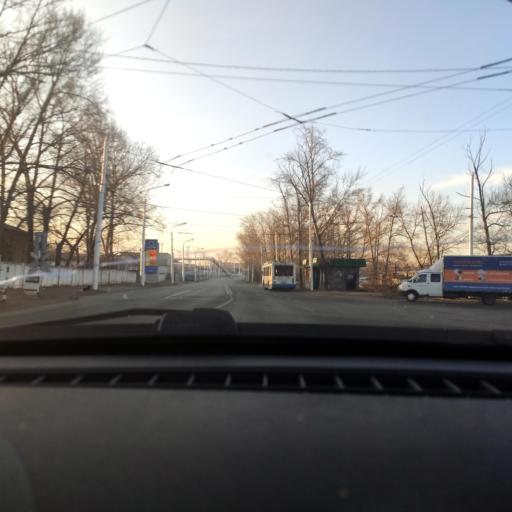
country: RU
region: Bashkortostan
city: Ufa
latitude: 54.8370
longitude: 56.0895
